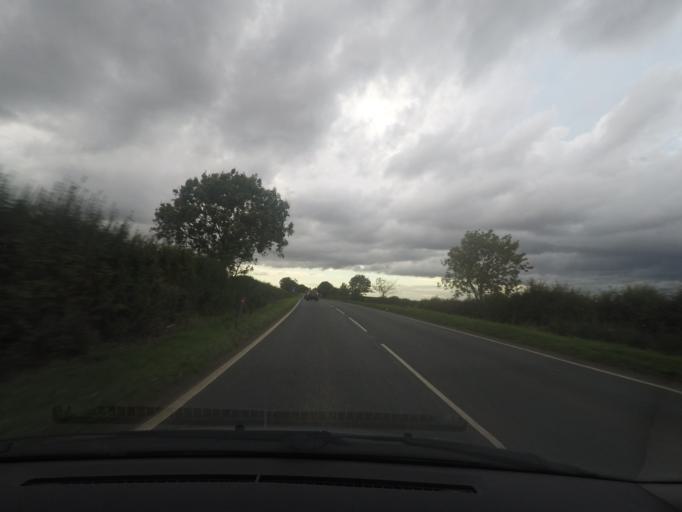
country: GB
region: England
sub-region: Lincolnshire
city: Louth
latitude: 53.3382
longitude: 0.0092
